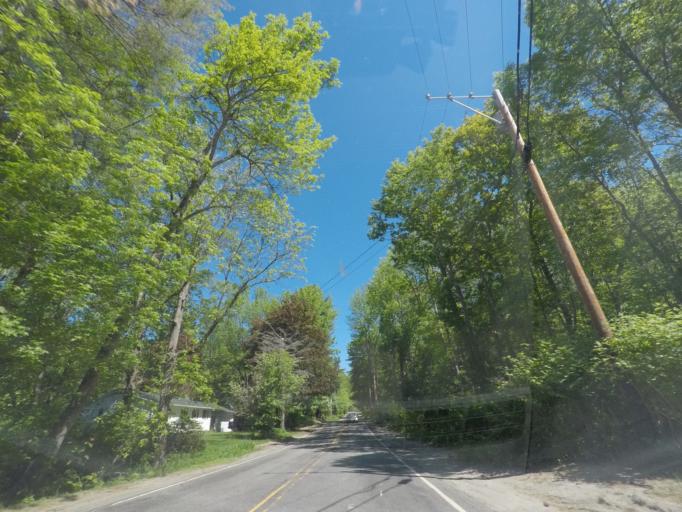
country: US
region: Maine
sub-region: Kennebec County
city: Manchester
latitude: 44.2829
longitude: -69.8894
